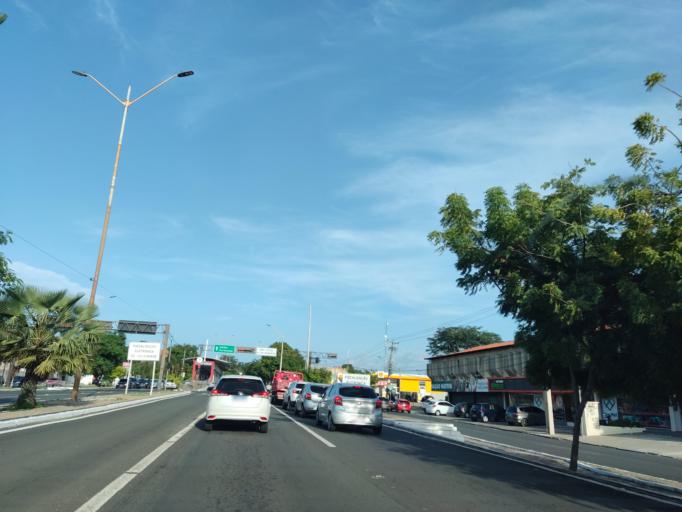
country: BR
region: Piaui
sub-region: Teresina
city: Teresina
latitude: -5.0810
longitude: -42.7785
